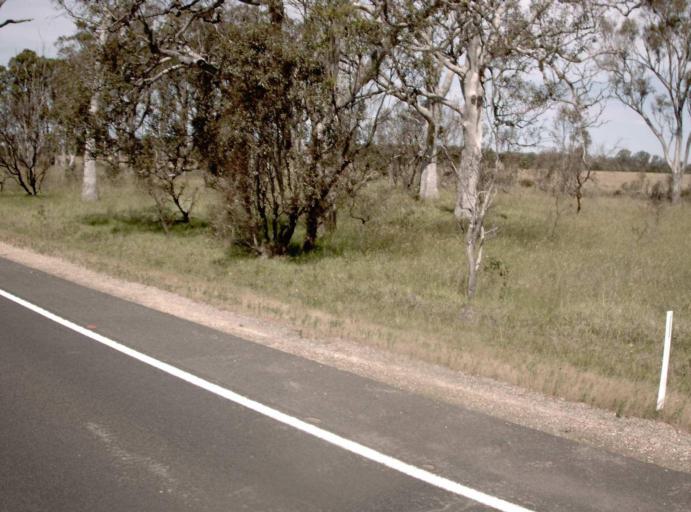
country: AU
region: Victoria
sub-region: East Gippsland
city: Bairnsdale
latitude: -37.8943
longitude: 147.3746
